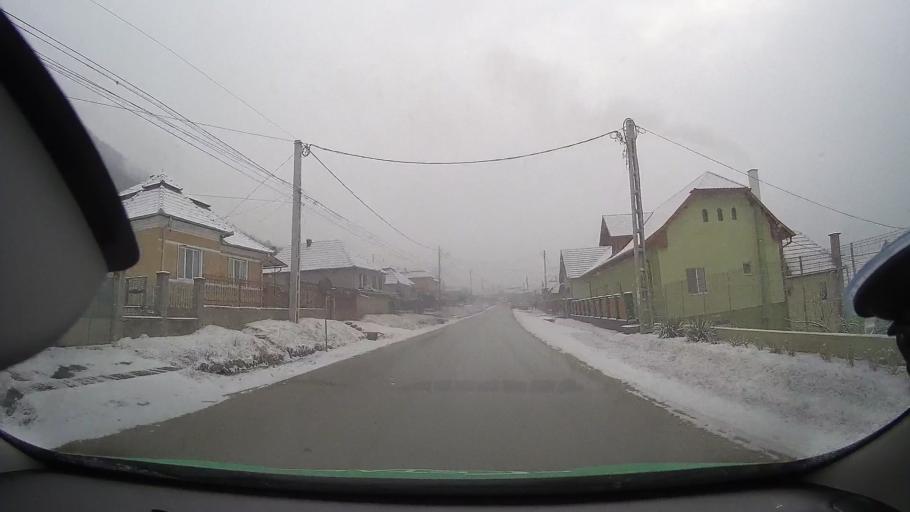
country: RO
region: Alba
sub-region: Comuna Lopadea Noua
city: Lopadea Noua
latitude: 46.2962
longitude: 23.8146
